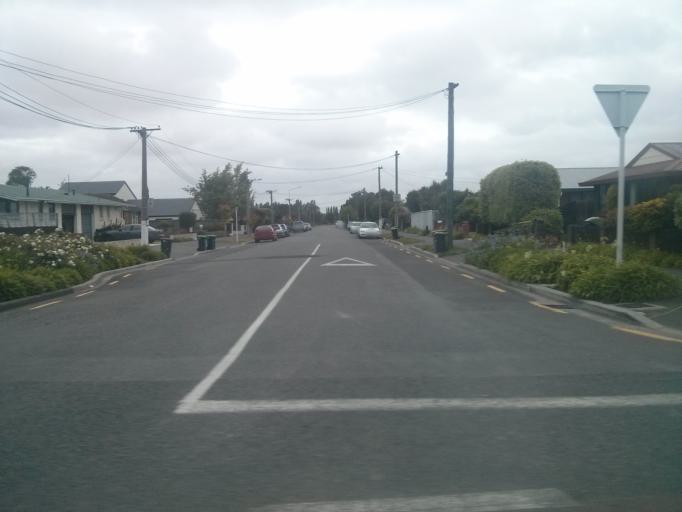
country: NZ
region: Canterbury
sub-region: Christchurch City
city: Christchurch
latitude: -43.4918
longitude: 172.6123
